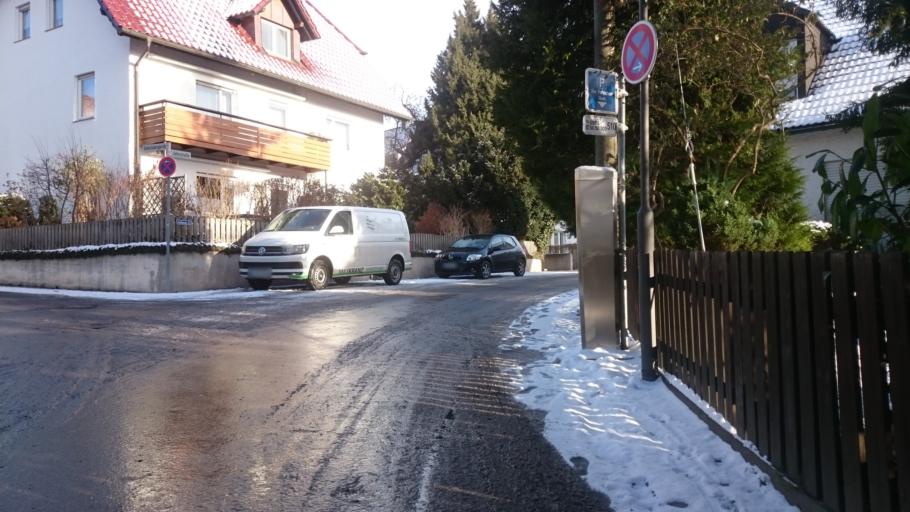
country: DE
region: Bavaria
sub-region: Swabia
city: Friedberg
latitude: 48.3533
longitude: 10.9834
